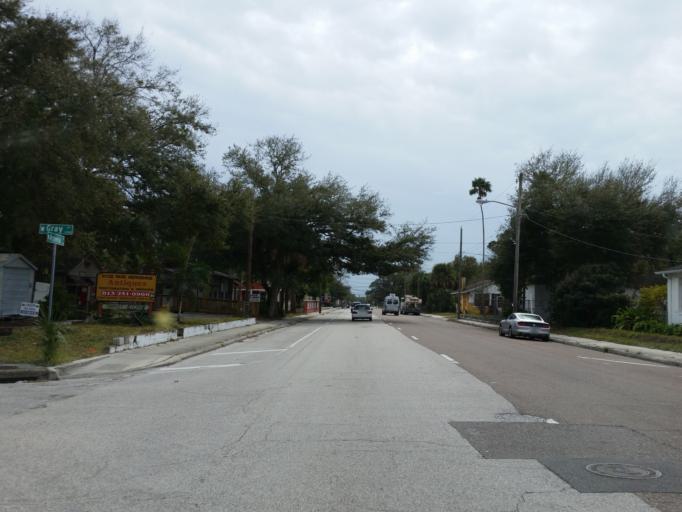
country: US
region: Florida
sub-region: Hillsborough County
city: Tampa
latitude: 27.9486
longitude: -82.4850
